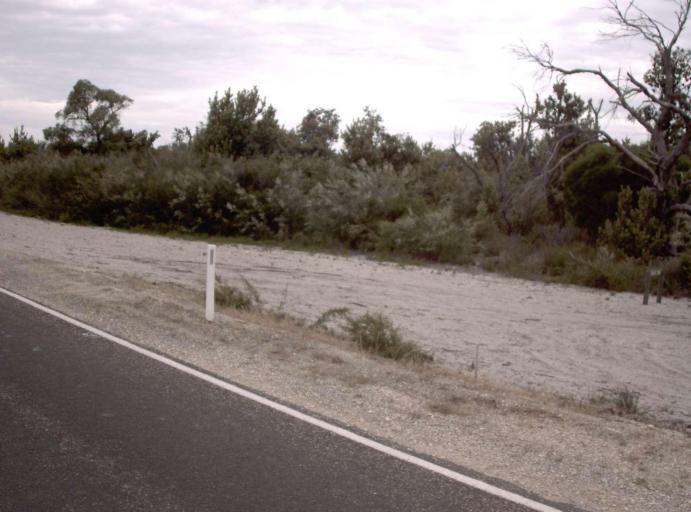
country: AU
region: Victoria
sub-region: Wellington
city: Sale
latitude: -38.1816
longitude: 147.3765
